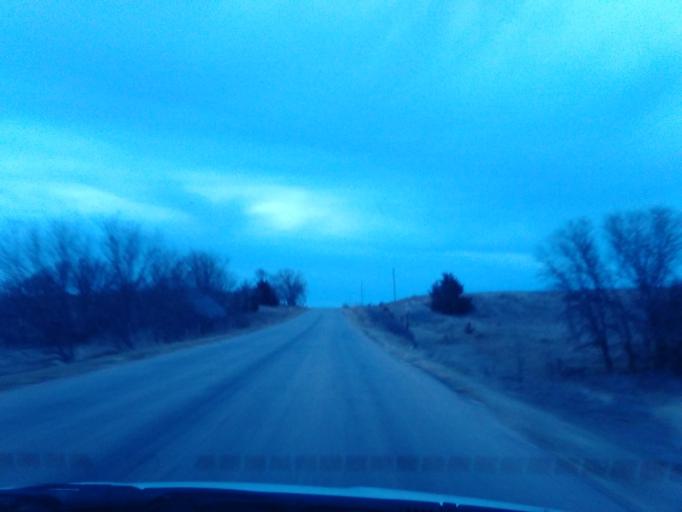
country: US
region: Nebraska
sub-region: Furnas County
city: Cambridge
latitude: 40.3607
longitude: -100.2124
